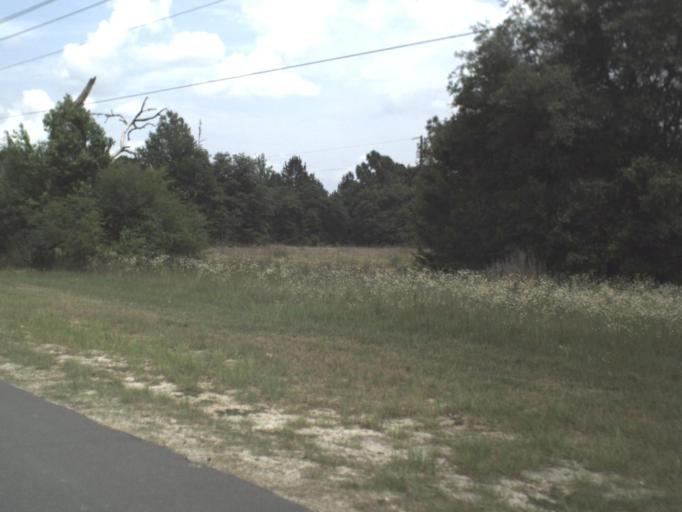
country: US
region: Florida
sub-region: Putnam County
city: Interlachen
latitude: 29.6235
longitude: -81.9325
